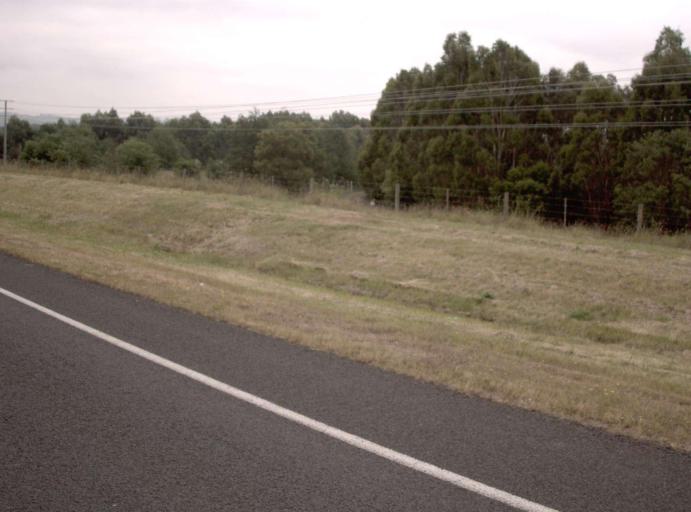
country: AU
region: Victoria
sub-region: Latrobe
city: Morwell
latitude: -38.2366
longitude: 146.3648
